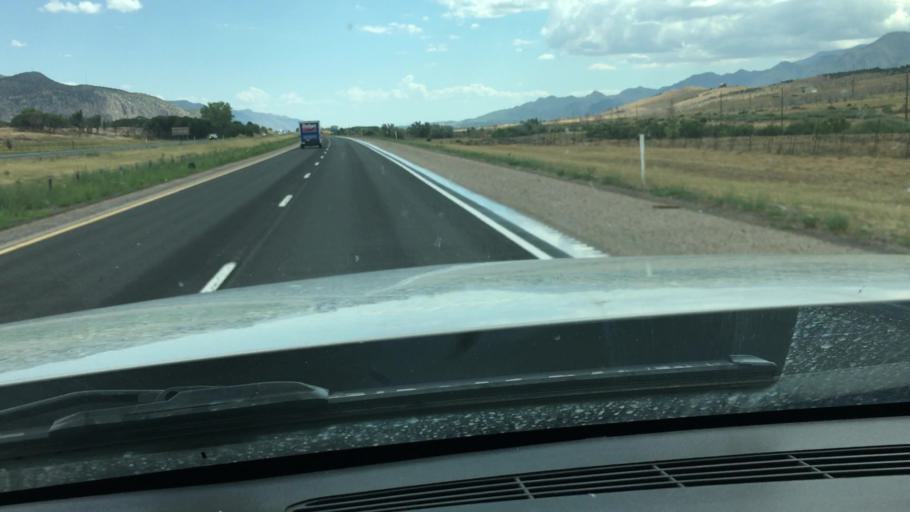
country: US
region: Utah
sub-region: Iron County
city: Cedar City
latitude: 37.5298
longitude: -113.2079
